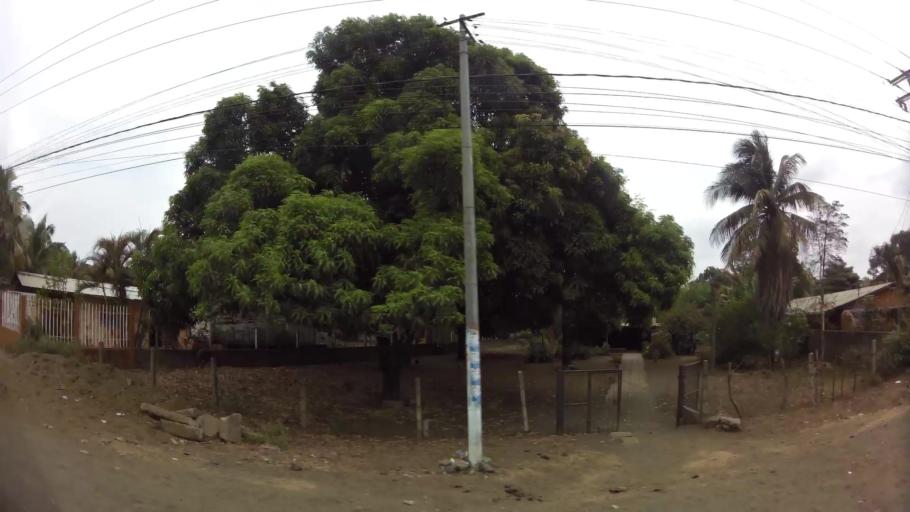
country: NI
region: Managua
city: Managua
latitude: 12.1250
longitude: -86.1751
